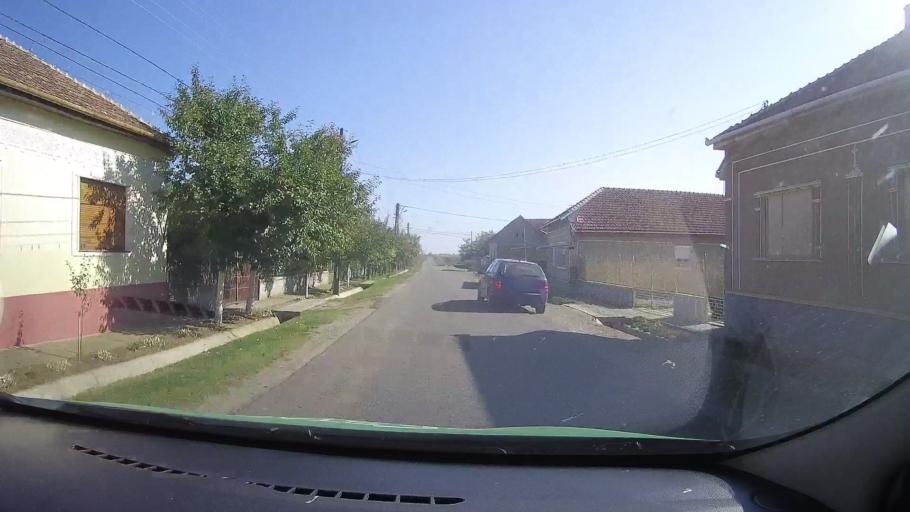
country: RO
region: Satu Mare
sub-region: Comuna Urziceni
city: Urziceni
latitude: 47.7355
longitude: 22.4088
